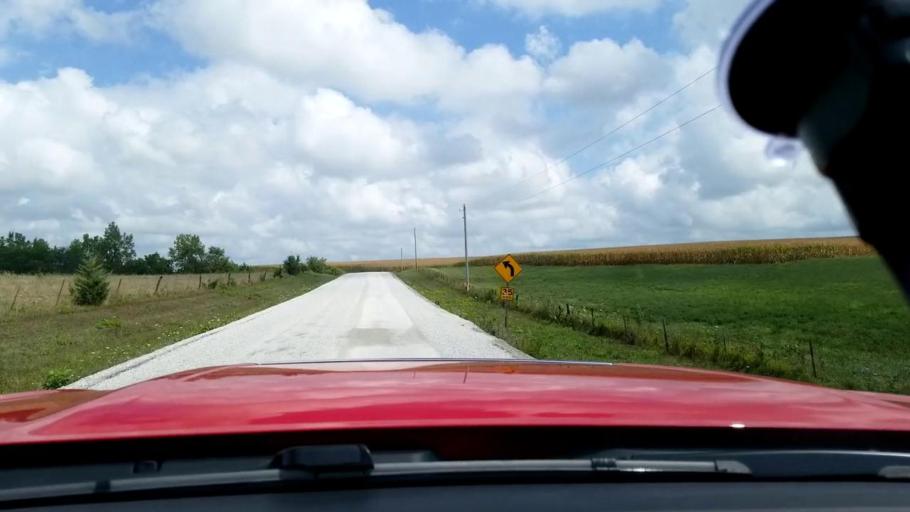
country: US
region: Iowa
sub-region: Decatur County
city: Lamoni
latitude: 40.6566
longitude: -94.0498
